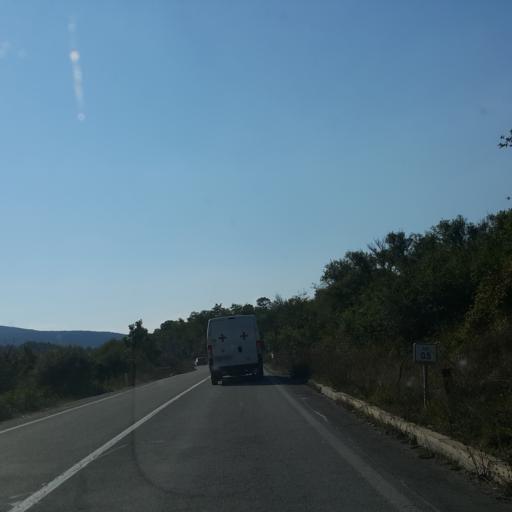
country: RS
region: Central Serbia
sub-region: Nisavski Okrug
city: Svrljig
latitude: 43.3992
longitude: 22.0752
